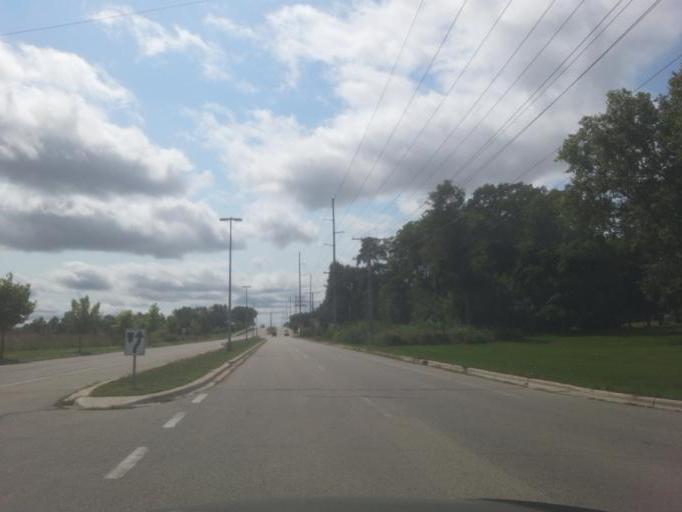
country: US
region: Wisconsin
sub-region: Dane County
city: Cottage Grove
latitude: 43.0939
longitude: -89.2669
